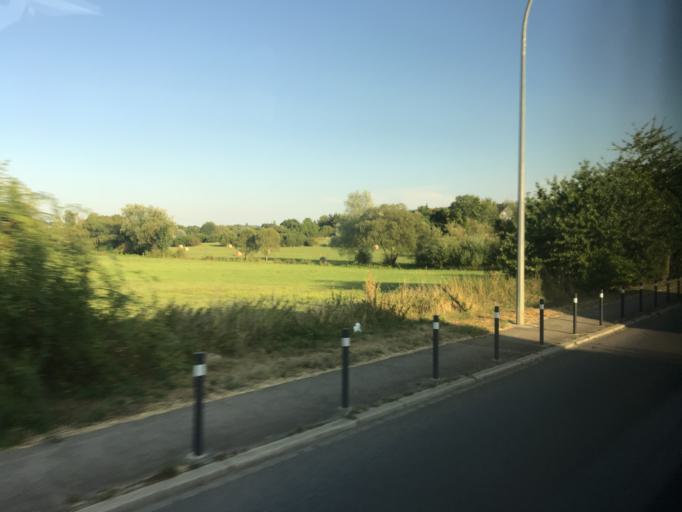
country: LU
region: Luxembourg
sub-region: Canton d'Esch-sur-Alzette
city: Frisange
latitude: 49.5207
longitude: 6.1862
